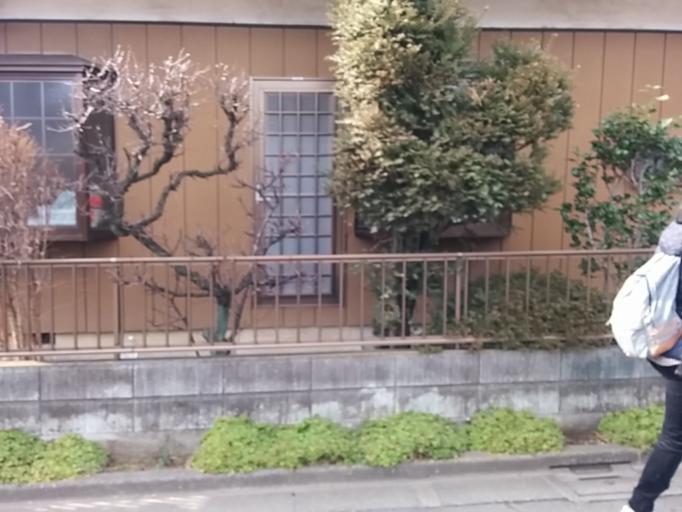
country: JP
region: Saitama
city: Kawagoe
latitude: 35.9269
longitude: 139.4903
